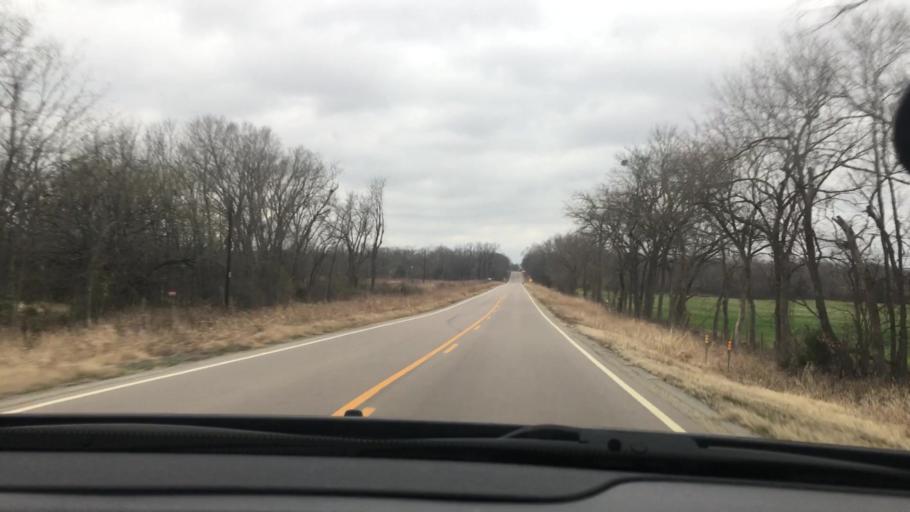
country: US
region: Oklahoma
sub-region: Coal County
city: Coalgate
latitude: 34.3708
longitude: -96.3496
